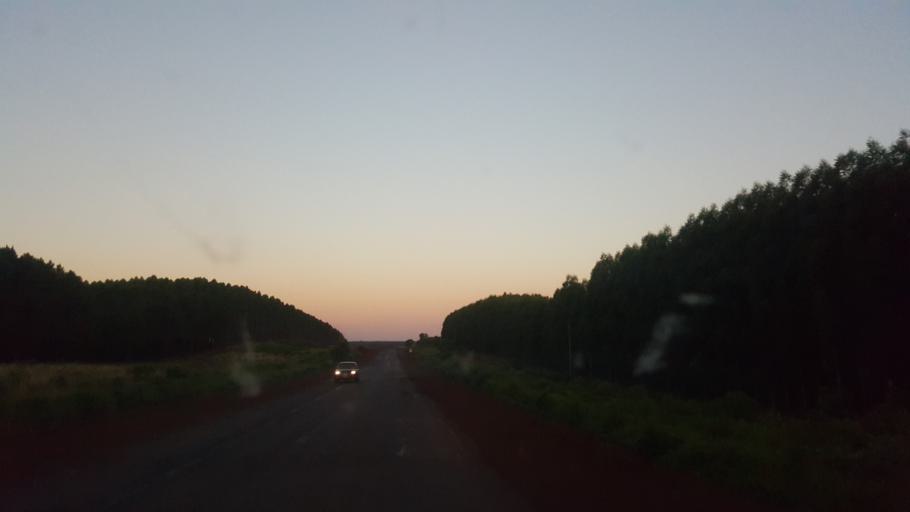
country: AR
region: Corrientes
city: Garruchos
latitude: -28.2451
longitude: -55.8375
